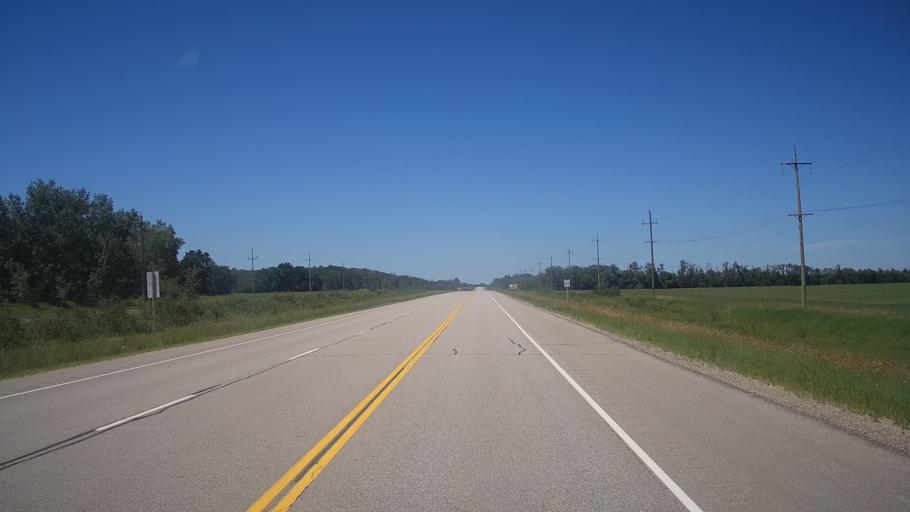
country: CA
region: Manitoba
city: Neepawa
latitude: 50.2253
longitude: -99.3444
